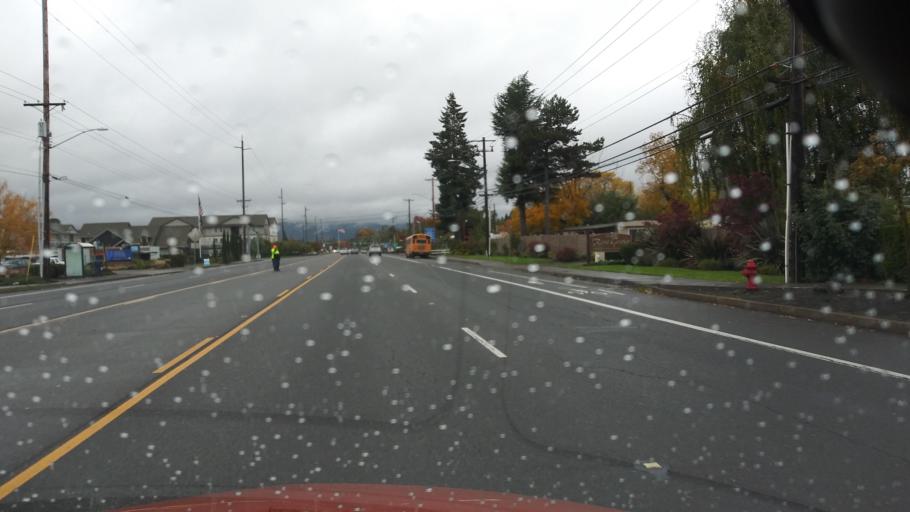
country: US
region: Oregon
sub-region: Washington County
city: Cornelius
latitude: 45.5203
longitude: -123.0779
